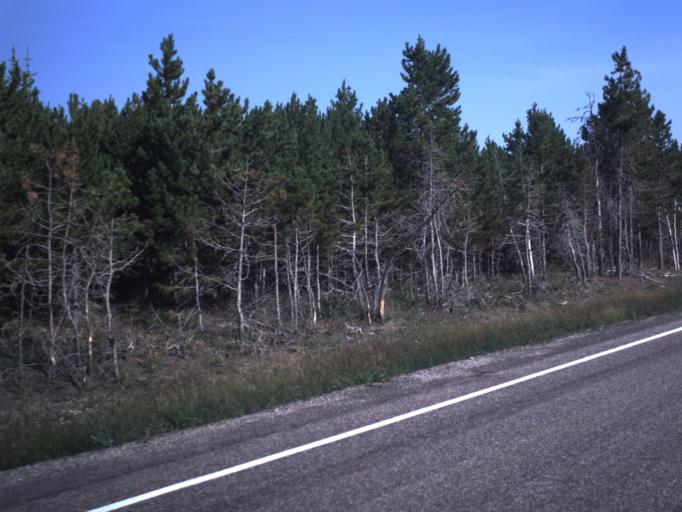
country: US
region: Utah
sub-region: Uintah County
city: Maeser
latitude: 40.7431
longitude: -109.4717
